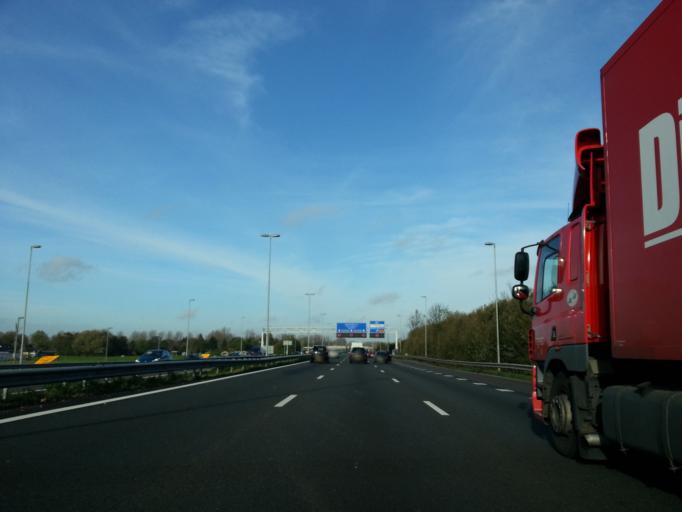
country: NL
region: South Holland
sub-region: Gemeente Schiedam
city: Schiedam
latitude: 51.9456
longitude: 4.4221
